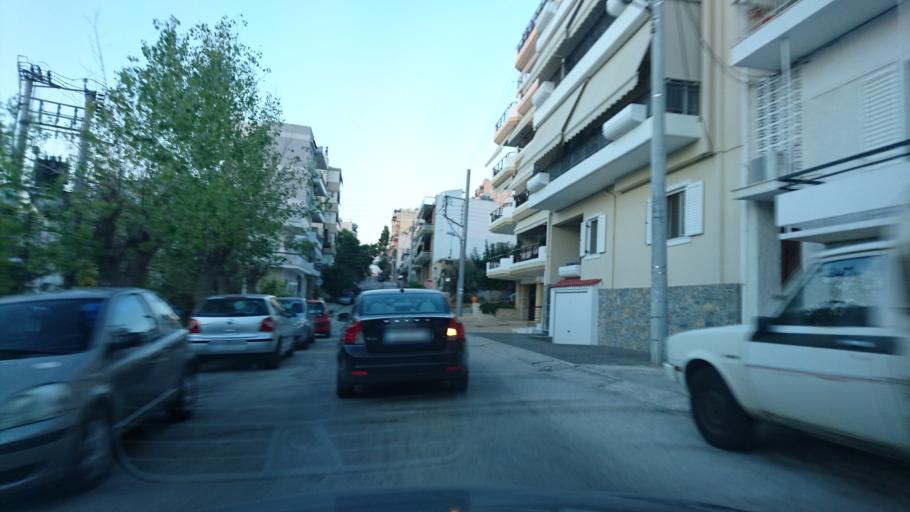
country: GR
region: Attica
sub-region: Nomarchia Athinas
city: Ilioupoli
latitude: 37.9396
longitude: 23.7662
